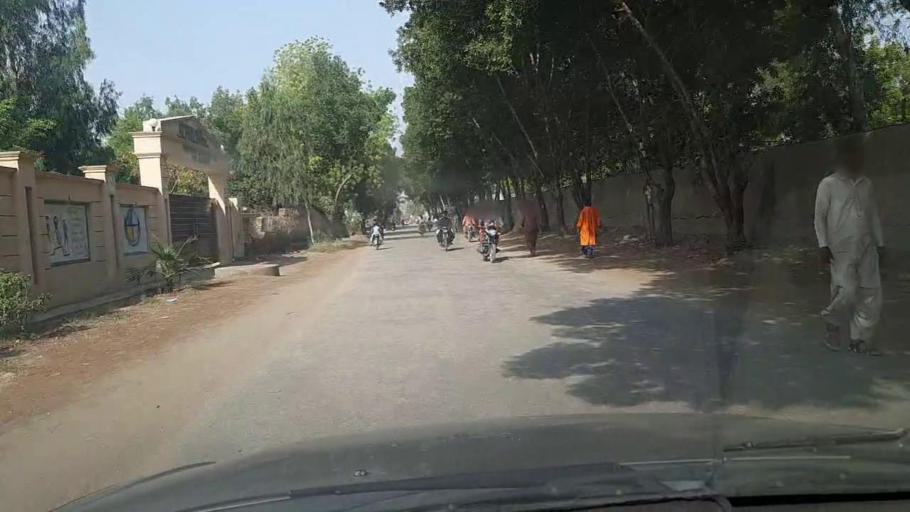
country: PK
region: Sindh
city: Mirpur Mathelo
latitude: 28.0230
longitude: 69.5551
